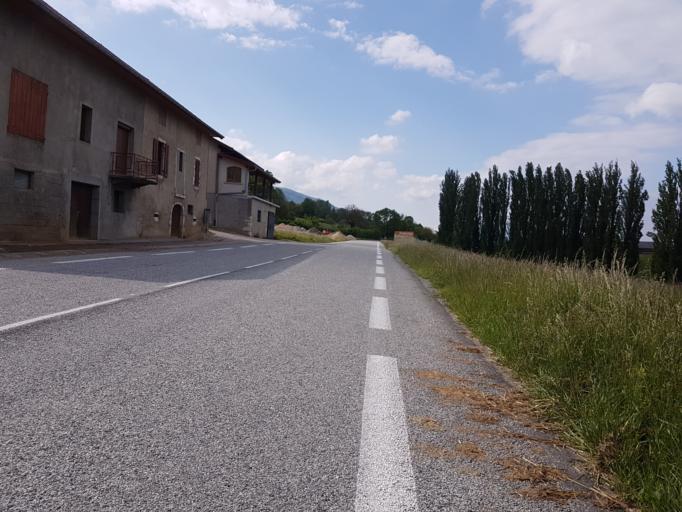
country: FR
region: Rhone-Alpes
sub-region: Departement de la Haute-Savoie
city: Moye
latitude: 45.9161
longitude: 5.8392
